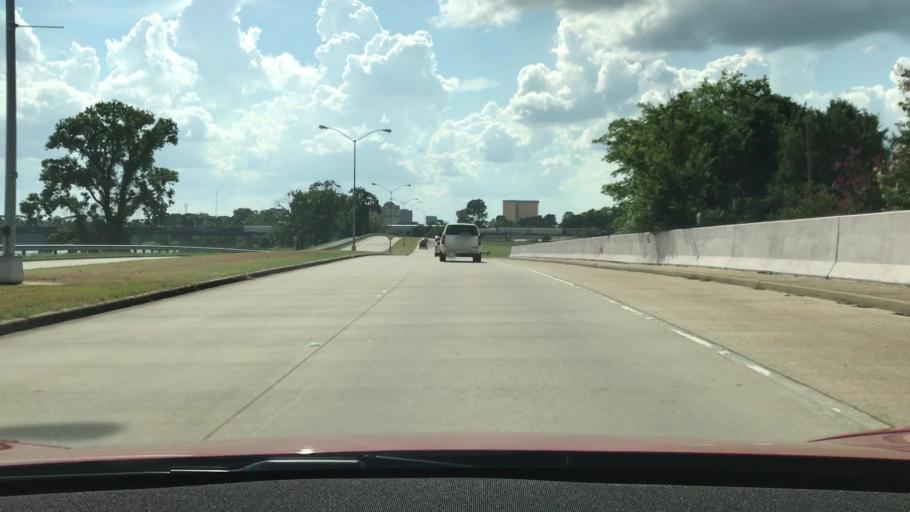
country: US
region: Louisiana
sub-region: Bossier Parish
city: Bossier City
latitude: 32.5098
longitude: -93.7181
